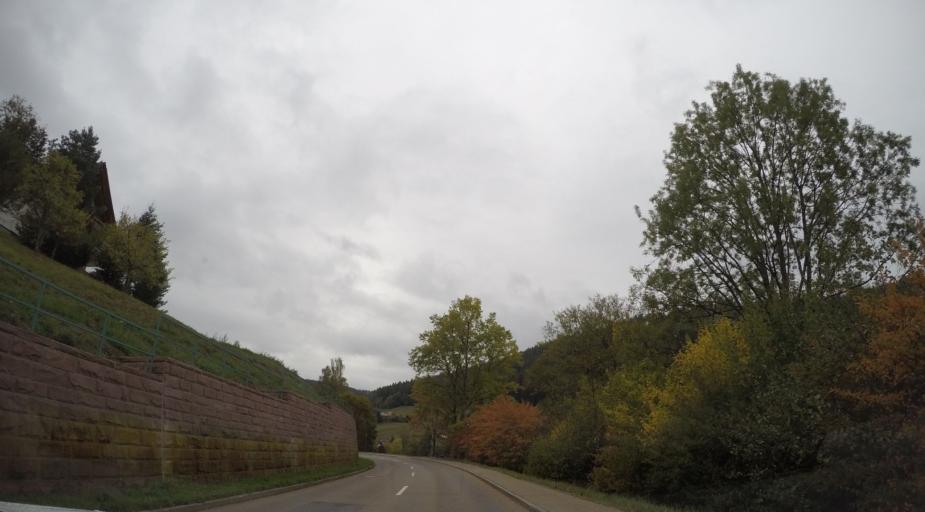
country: DE
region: Baden-Wuerttemberg
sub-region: Karlsruhe Region
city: Baiersbronn
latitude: 48.5333
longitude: 8.3612
